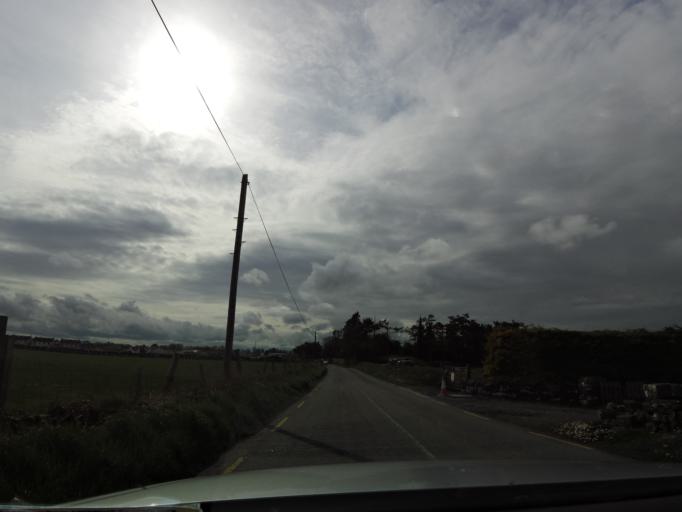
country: IE
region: Leinster
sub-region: Laois
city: Rathdowney
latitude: 52.7238
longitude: -7.5708
